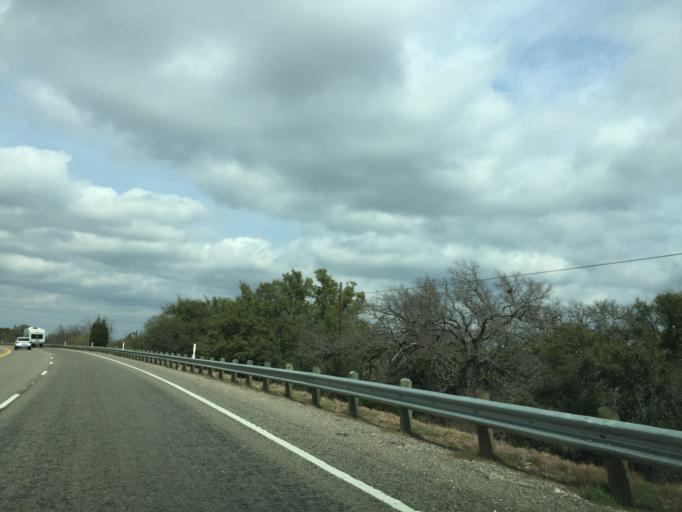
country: US
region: Texas
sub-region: Travis County
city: Briarcliff
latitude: 30.4506
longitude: -98.1487
